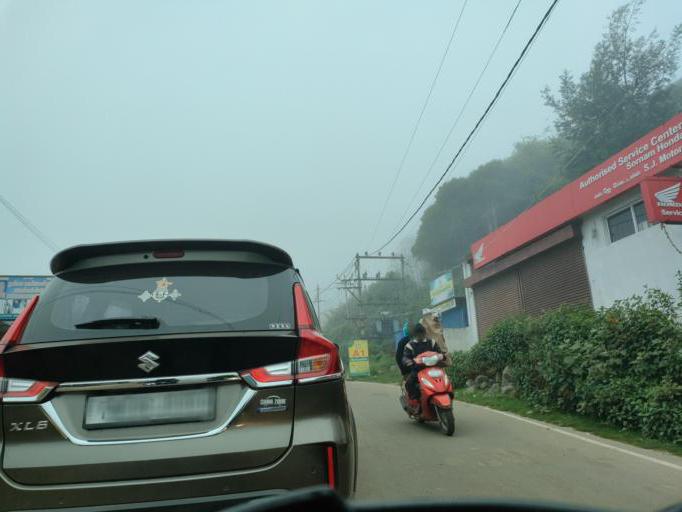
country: IN
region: Tamil Nadu
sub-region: Dindigul
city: Kodaikanal
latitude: 10.2310
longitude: 77.4715
